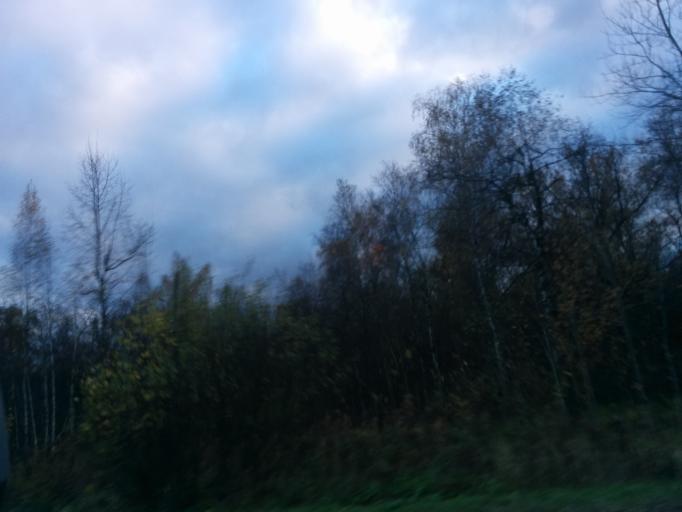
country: RU
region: Moscow
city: Annino
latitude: 55.5442
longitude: 37.6200
